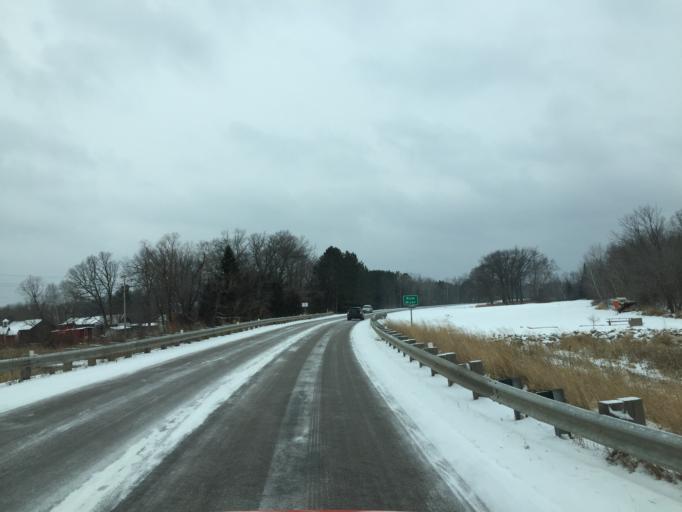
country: US
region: Minnesota
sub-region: Mille Lacs County
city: Vineland
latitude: 46.0690
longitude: -93.6795
